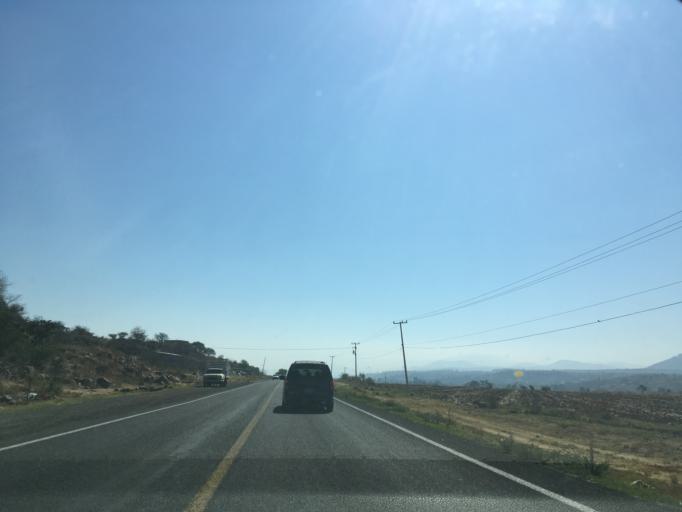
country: MX
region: Michoacan
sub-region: Indaparapeo
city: San Lucas Pio
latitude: 19.7945
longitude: -100.9437
